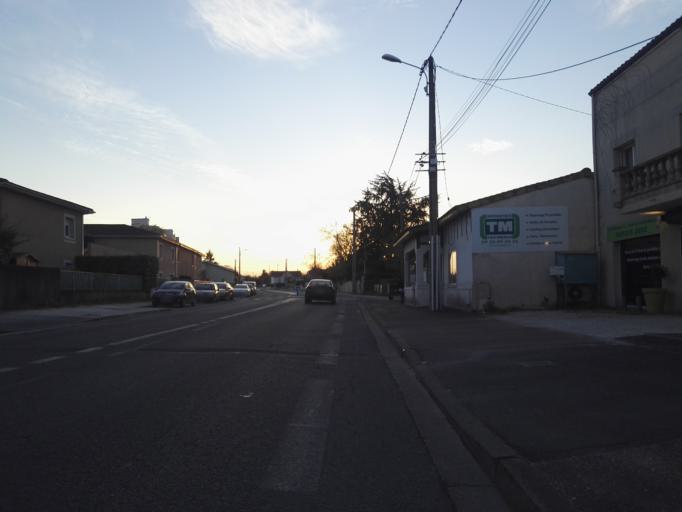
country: FR
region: Aquitaine
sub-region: Departement de la Gironde
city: Pessac
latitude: 44.8093
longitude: -0.6331
